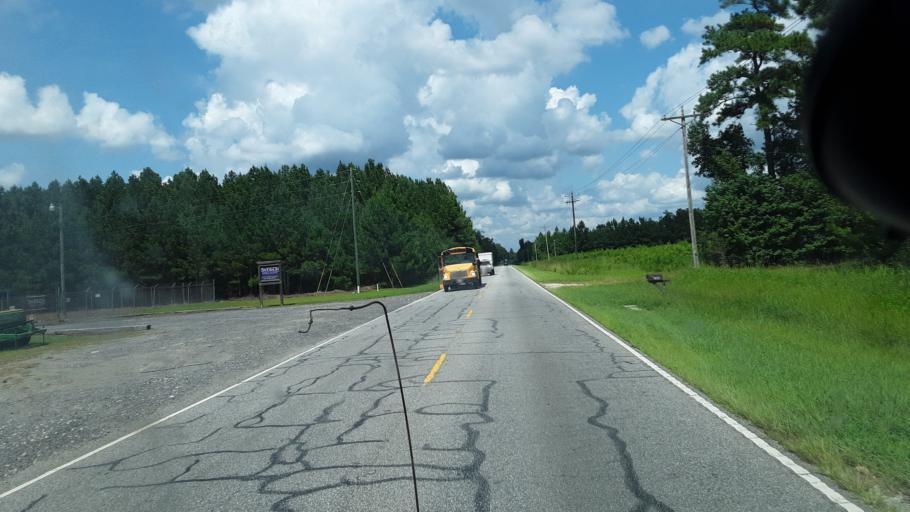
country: US
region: South Carolina
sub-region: Williamsburg County
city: Andrews
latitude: 33.6088
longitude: -79.4380
